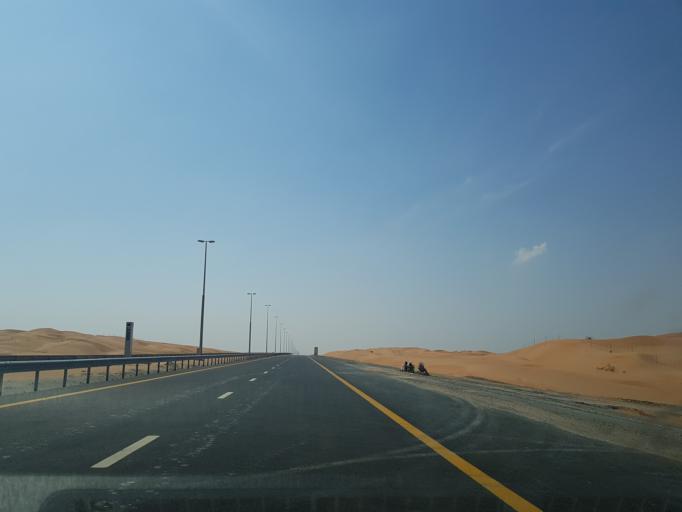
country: AE
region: Ash Shariqah
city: Adh Dhayd
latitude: 25.2519
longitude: 55.7809
